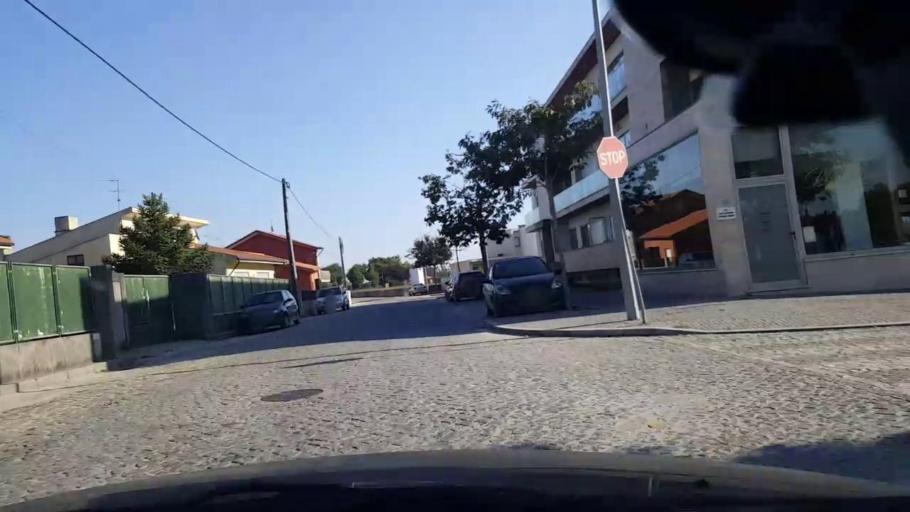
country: PT
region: Porto
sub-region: Vila do Conde
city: Arvore
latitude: 41.3523
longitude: -8.7203
